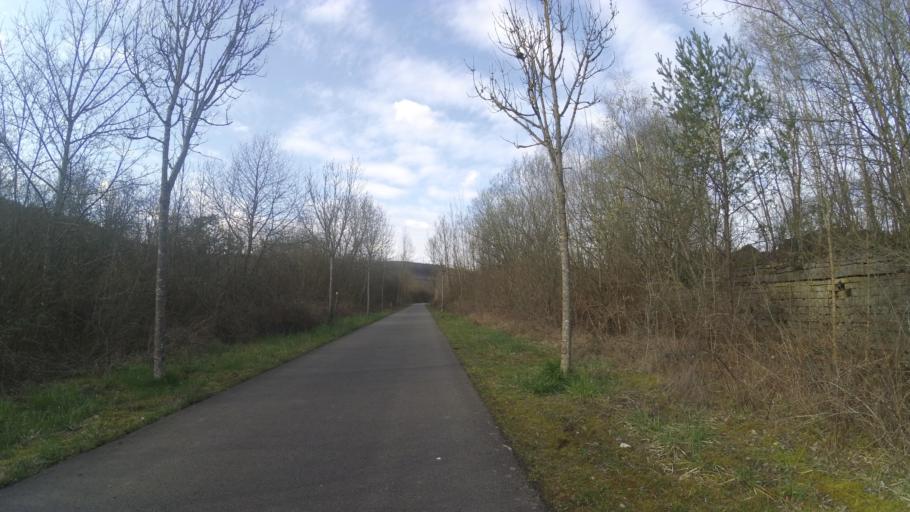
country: DE
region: Saarland
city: Gersheim
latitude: 49.1525
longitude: 7.2083
